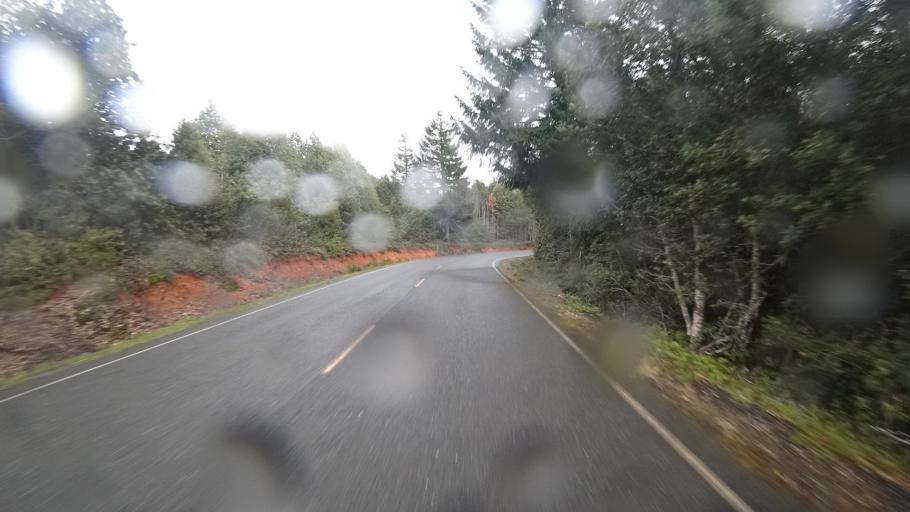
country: US
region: California
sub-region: Humboldt County
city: Willow Creek
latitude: 41.1870
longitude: -123.8155
